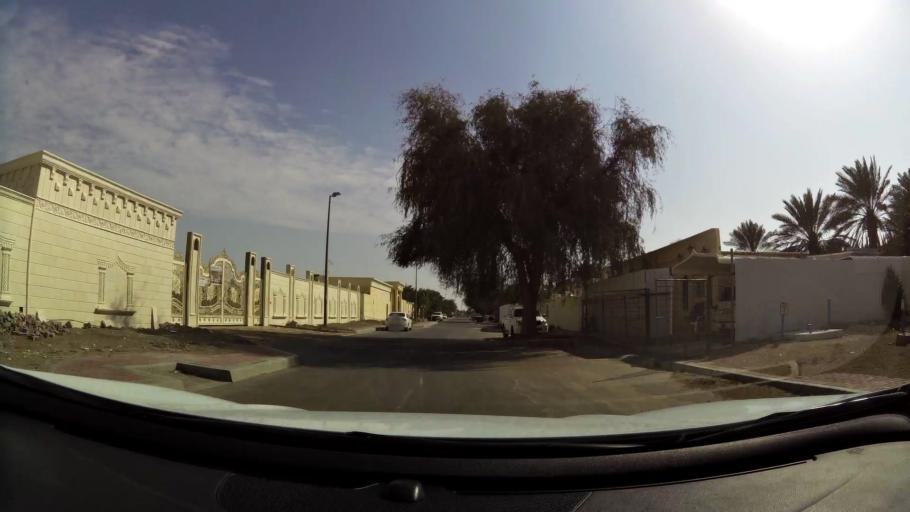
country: AE
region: Abu Dhabi
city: Al Ain
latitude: 24.0970
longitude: 55.9229
